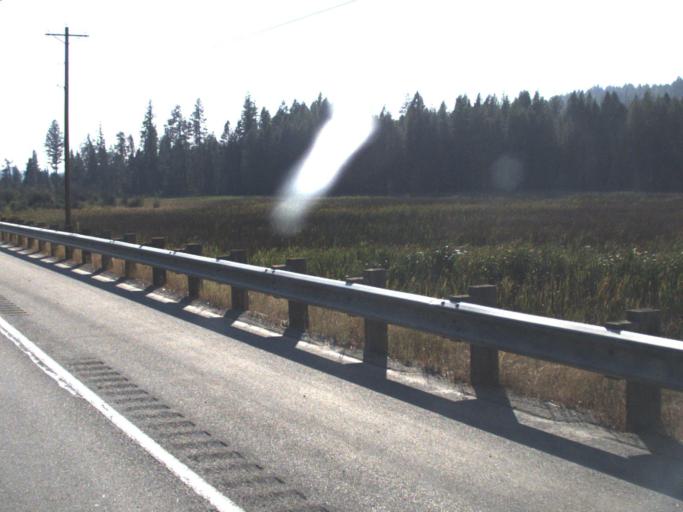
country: US
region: Washington
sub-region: Pend Oreille County
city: Newport
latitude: 48.1656
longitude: -117.0817
